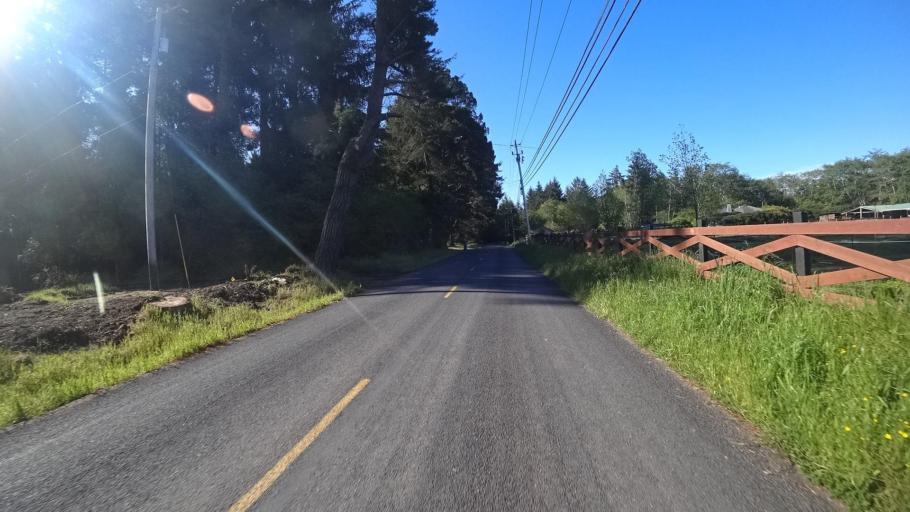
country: US
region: California
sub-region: Humboldt County
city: McKinleyville
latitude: 40.9880
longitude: -124.1005
